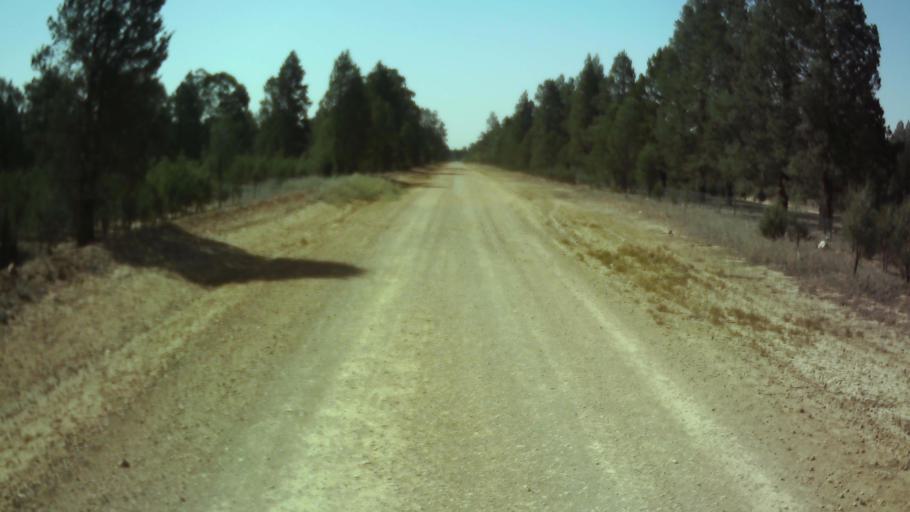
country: AU
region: New South Wales
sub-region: Weddin
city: Grenfell
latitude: -33.9168
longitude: 147.9223
